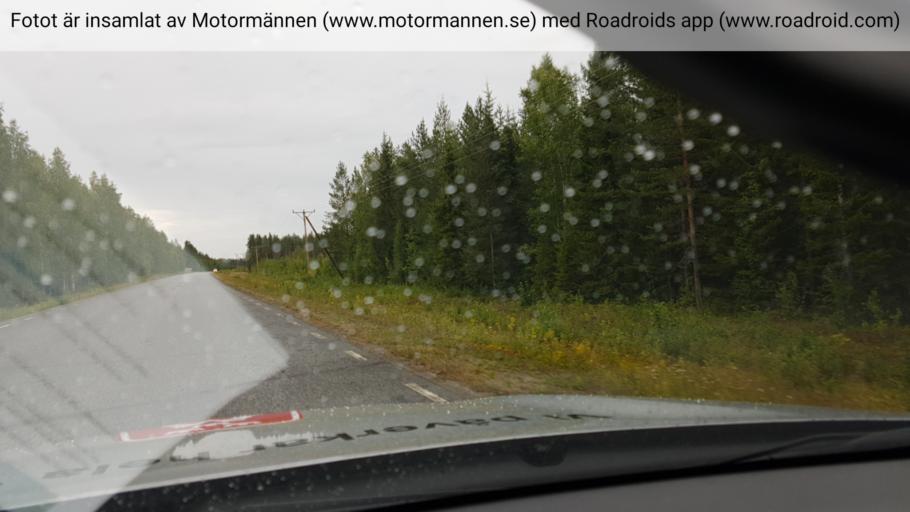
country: SE
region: Norrbotten
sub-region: Bodens Kommun
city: Boden
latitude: 65.8340
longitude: 21.4980
